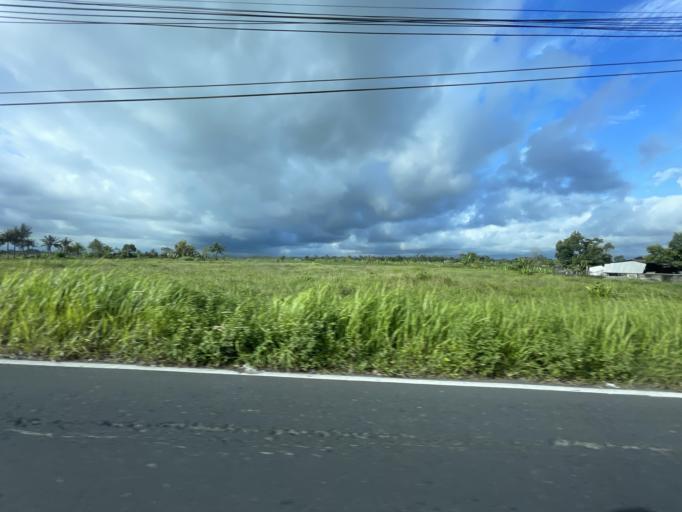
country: ID
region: Bali
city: Banjar Desa
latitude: -8.5798
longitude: 115.2507
